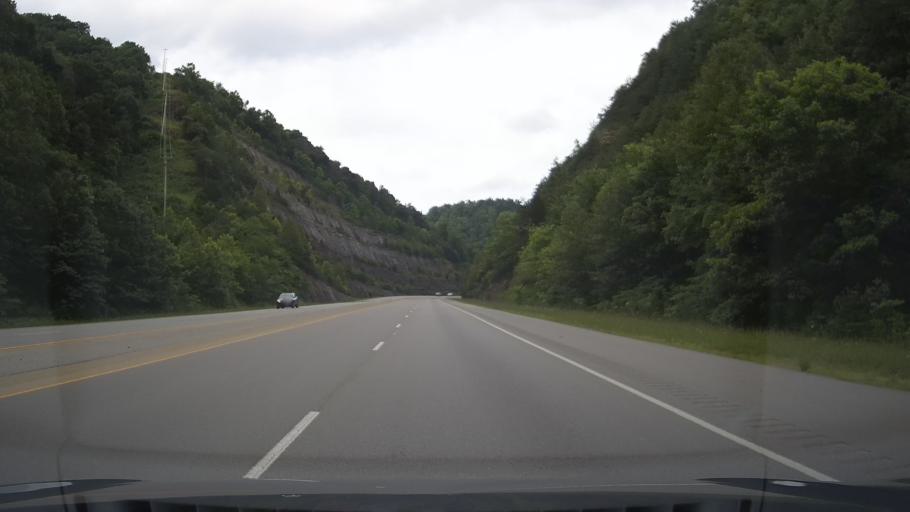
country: US
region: Kentucky
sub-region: Pike County
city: Pikeville
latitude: 37.4122
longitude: -82.5318
